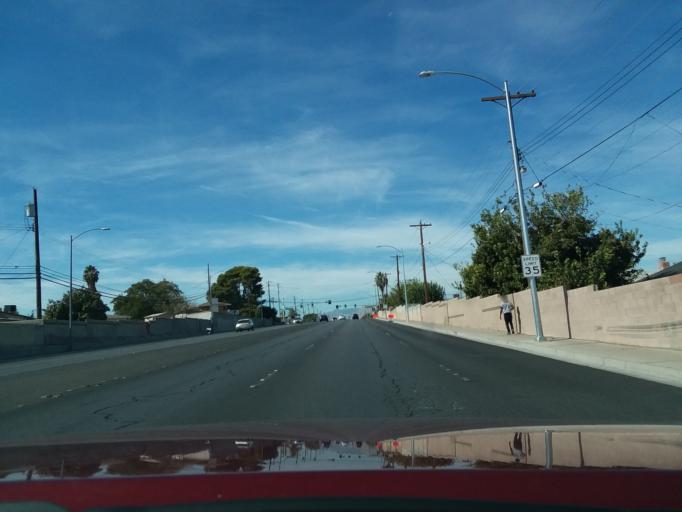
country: US
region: Nevada
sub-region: Clark County
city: Las Vegas
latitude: 36.1958
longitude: -115.1452
